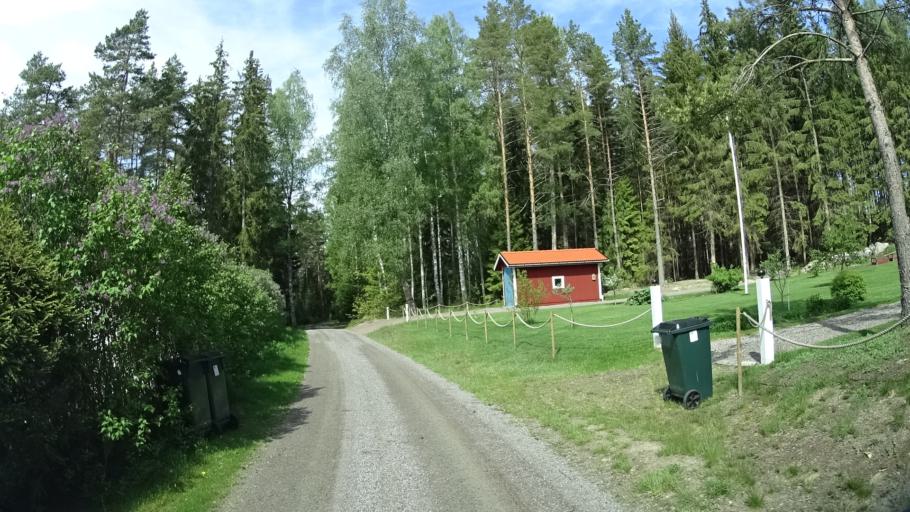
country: SE
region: OEstergoetland
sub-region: Finspangs Kommun
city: Finspang
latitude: 58.7909
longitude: 15.8673
